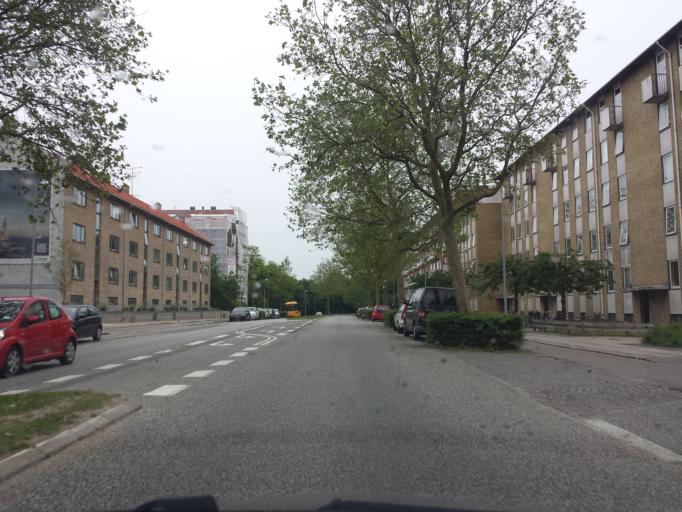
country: DK
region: Capital Region
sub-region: Lyngby-Tarbaek Kommune
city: Kongens Lyngby
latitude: 55.7647
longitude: 12.5104
